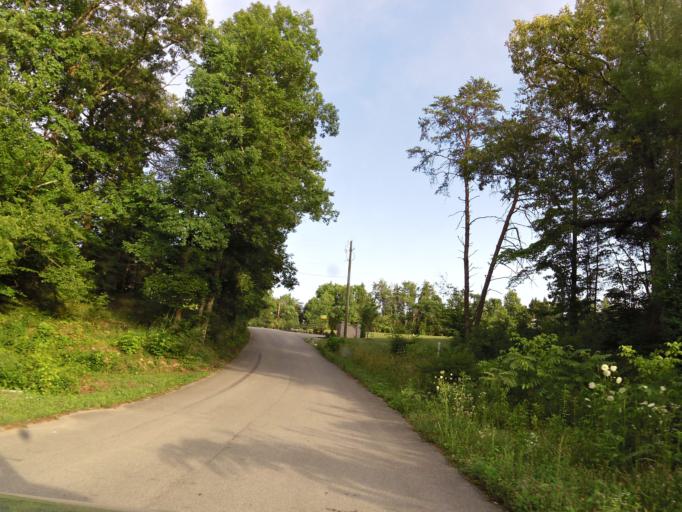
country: US
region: Tennessee
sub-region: Knox County
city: Knoxville
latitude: 35.9131
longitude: -83.8342
